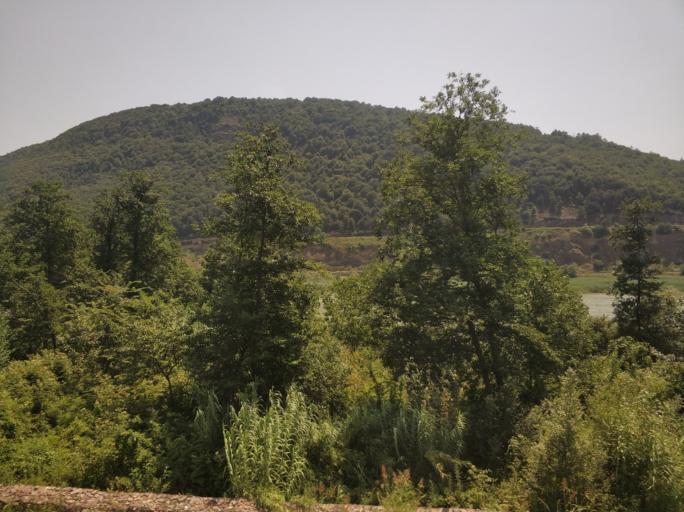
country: IR
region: Gilan
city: Pa'in-e Bazar-e Rudbar
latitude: 36.9775
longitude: 49.5547
